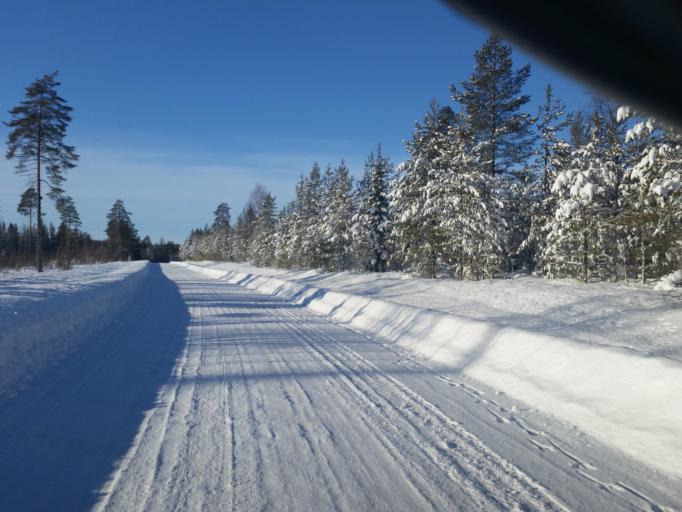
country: SE
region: Vaesterbotten
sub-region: Skelleftea Kommun
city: Backa
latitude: 65.2009
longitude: 20.9979
